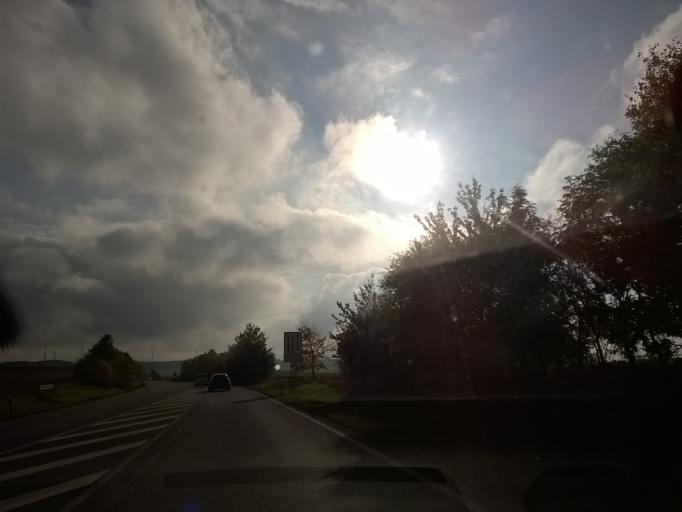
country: DE
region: Thuringia
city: Nordhausen
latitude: 51.4676
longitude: 10.8004
